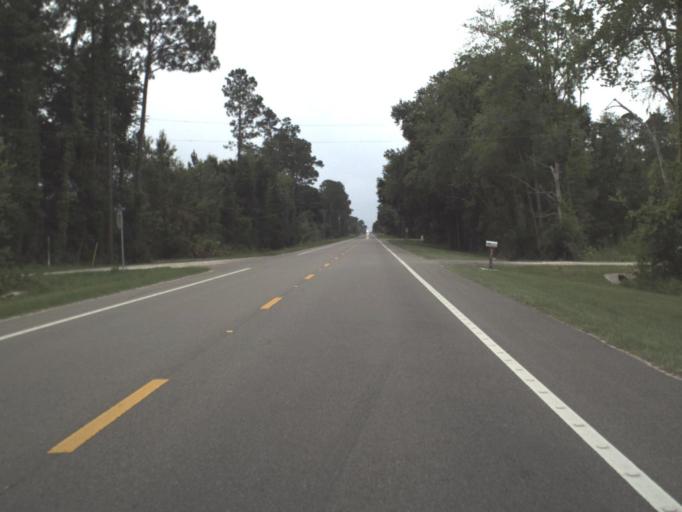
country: US
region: Florida
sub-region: Bradford County
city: Starke
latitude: 29.9132
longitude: -82.0936
